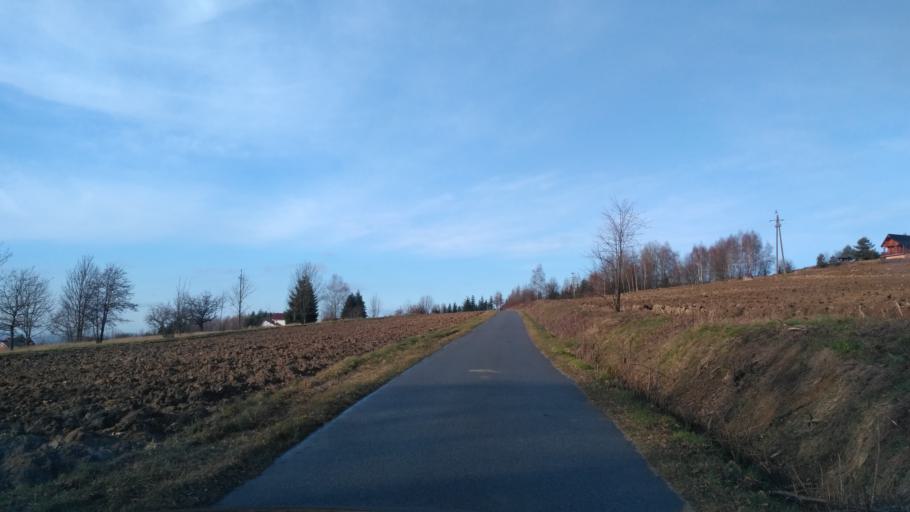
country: PL
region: Subcarpathian Voivodeship
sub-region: Powiat krosnienski
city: Korczyna
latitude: 49.7481
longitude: 21.7980
